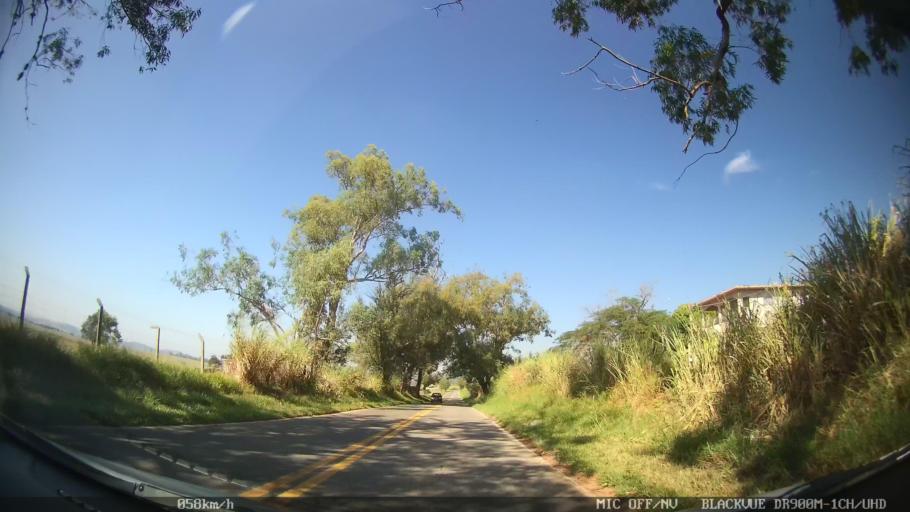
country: BR
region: Sao Paulo
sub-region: Valinhos
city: Valinhos
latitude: -23.0260
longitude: -47.0995
